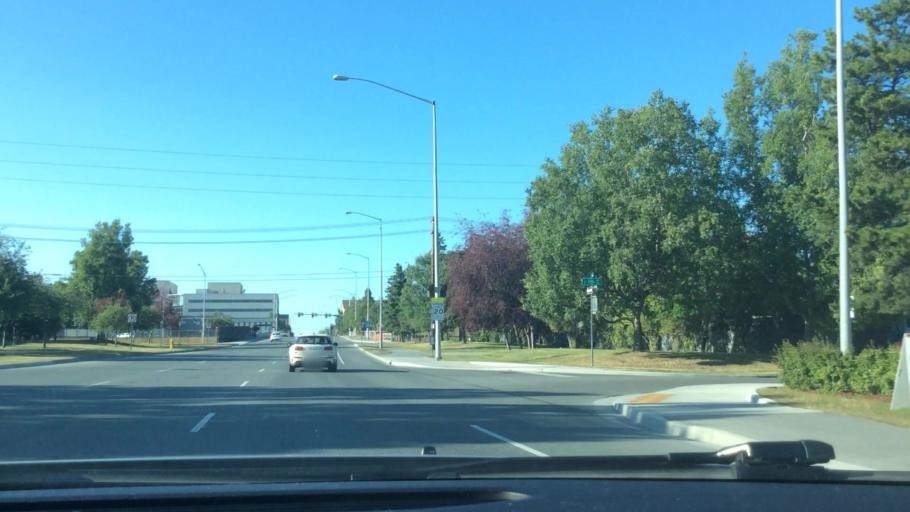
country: US
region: Alaska
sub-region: Anchorage Municipality
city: Anchorage
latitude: 61.2116
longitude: -149.8824
